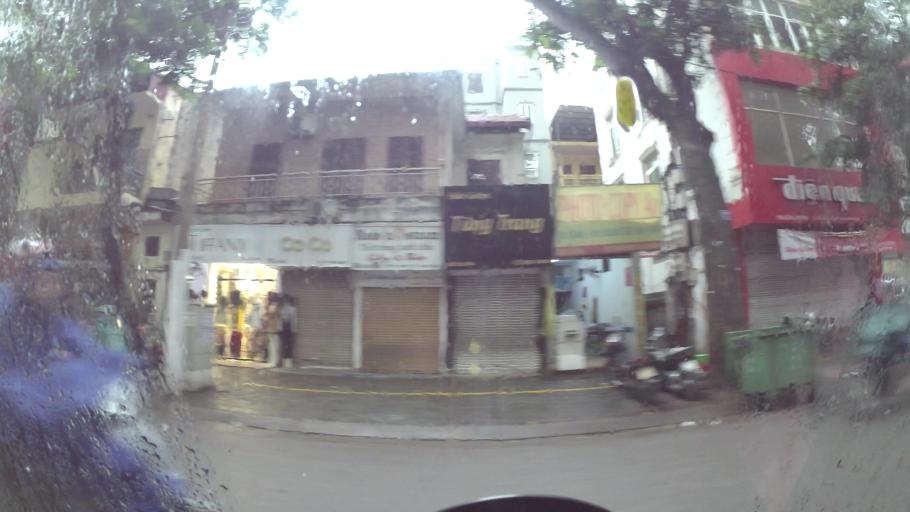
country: VN
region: Ha Noi
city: Hai BaTrung
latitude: 21.0162
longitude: 105.8562
